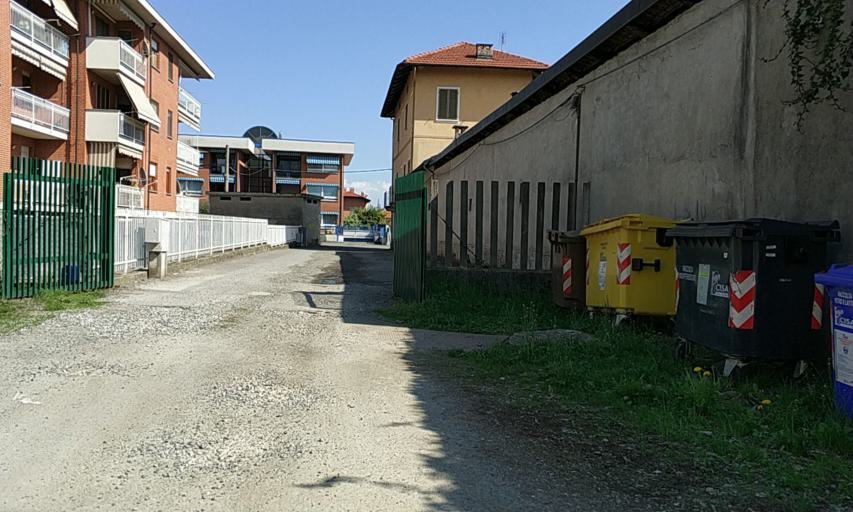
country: IT
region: Piedmont
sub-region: Provincia di Torino
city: Nole
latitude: 45.2417
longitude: 7.5685
